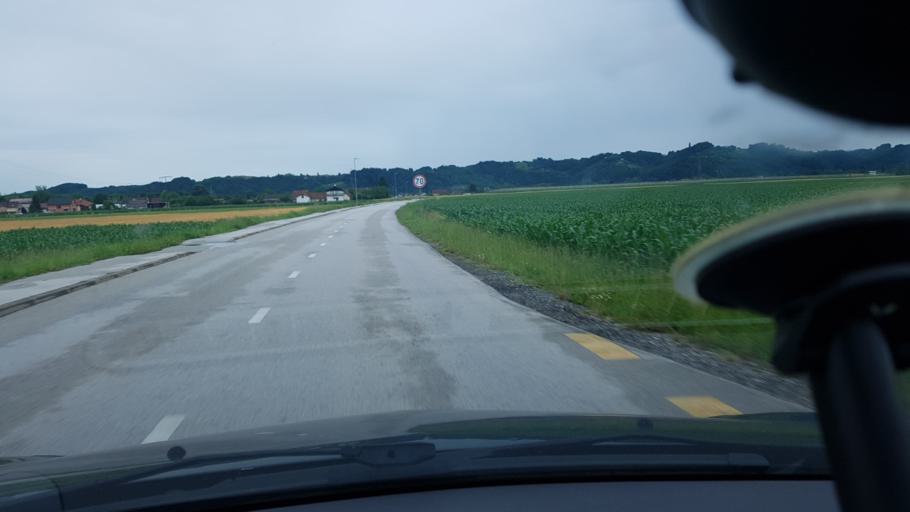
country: SI
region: Videm
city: Videm pri Ptuju
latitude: 46.3815
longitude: 15.8804
